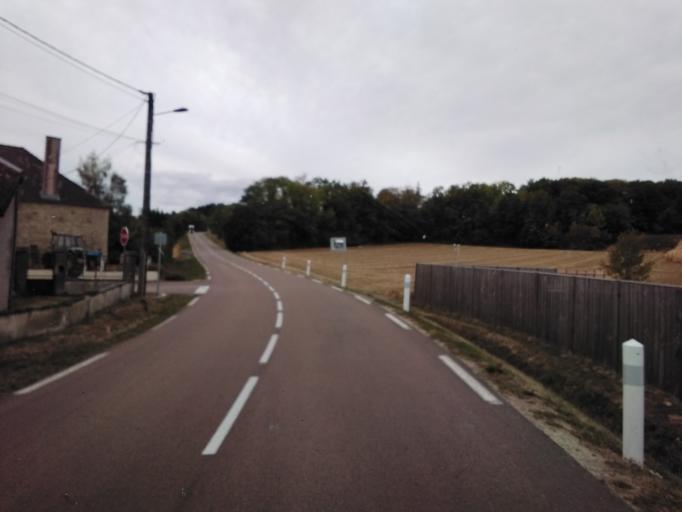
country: FR
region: Champagne-Ardenne
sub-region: Departement de l'Aube
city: Vendeuvre-sur-Barse
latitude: 48.1921
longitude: 4.4397
